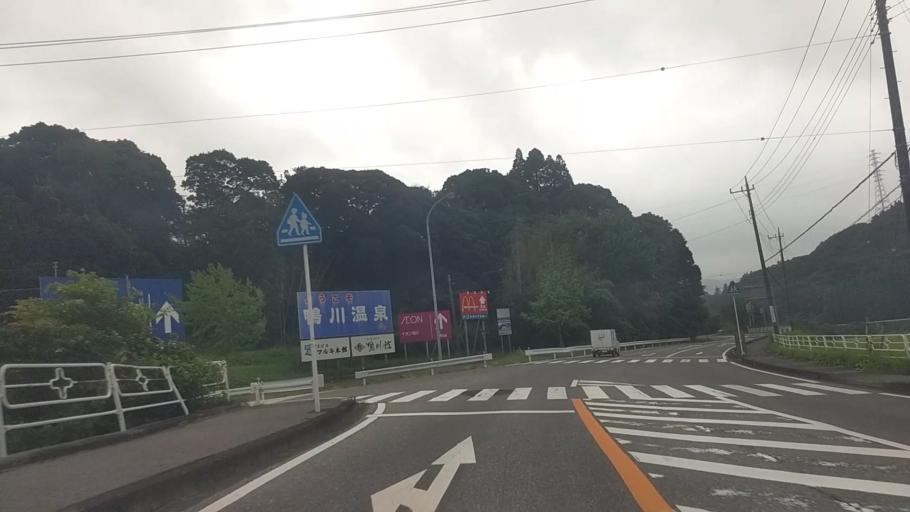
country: JP
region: Chiba
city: Kawaguchi
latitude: 35.1434
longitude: 140.0697
